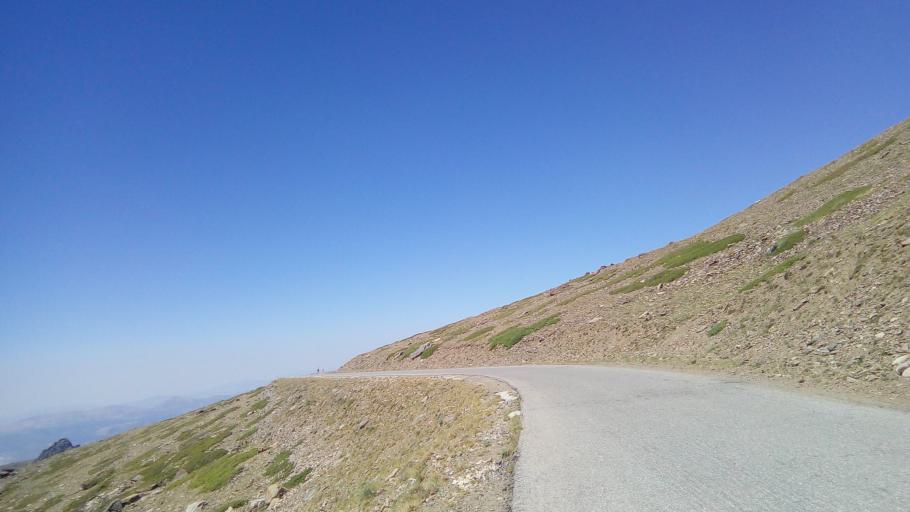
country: ES
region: Andalusia
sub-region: Provincia de Granada
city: Guejar-Sierra
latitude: 37.0791
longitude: -3.3838
